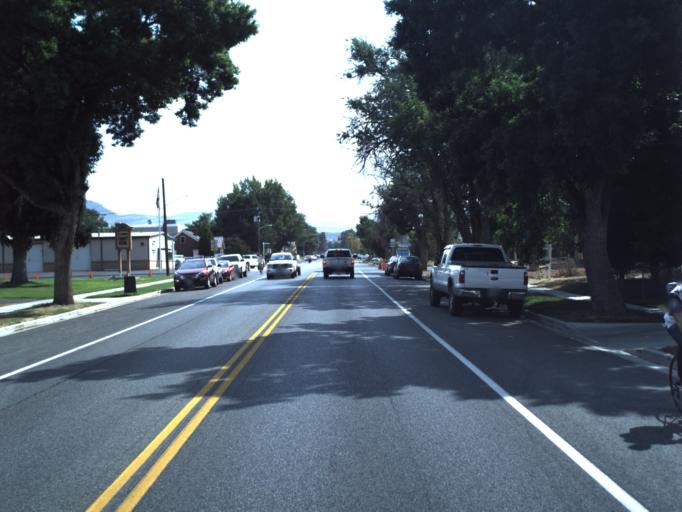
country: US
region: Utah
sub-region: Wasatch County
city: Heber
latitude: 40.5064
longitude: -111.4164
